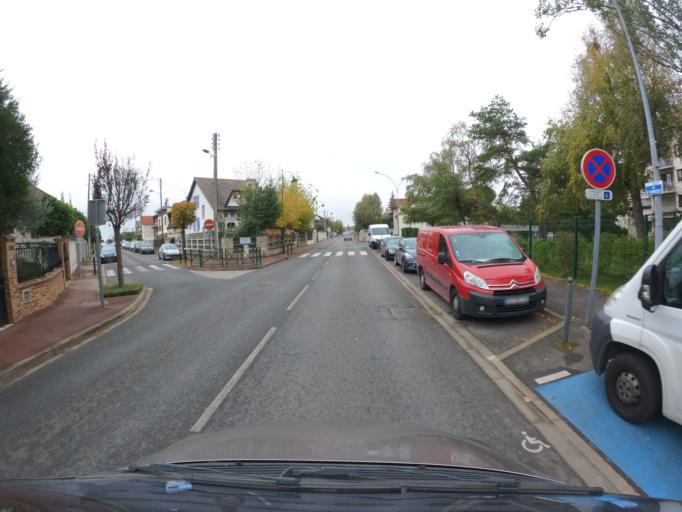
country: FR
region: Ile-de-France
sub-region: Departement du Val-de-Marne
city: Chennevieres-sur-Marne
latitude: 48.7892
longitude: 2.5315
